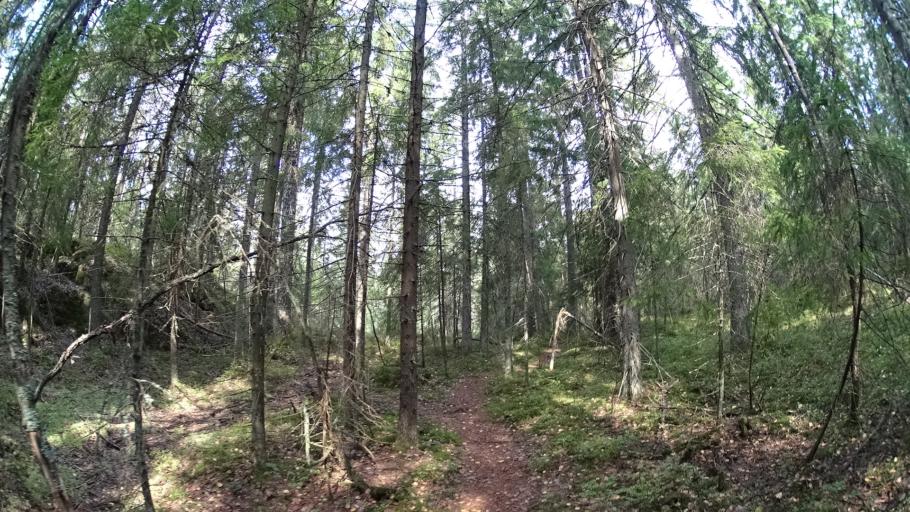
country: FI
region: Uusimaa
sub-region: Helsinki
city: Espoo
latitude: 60.3017
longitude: 24.5862
